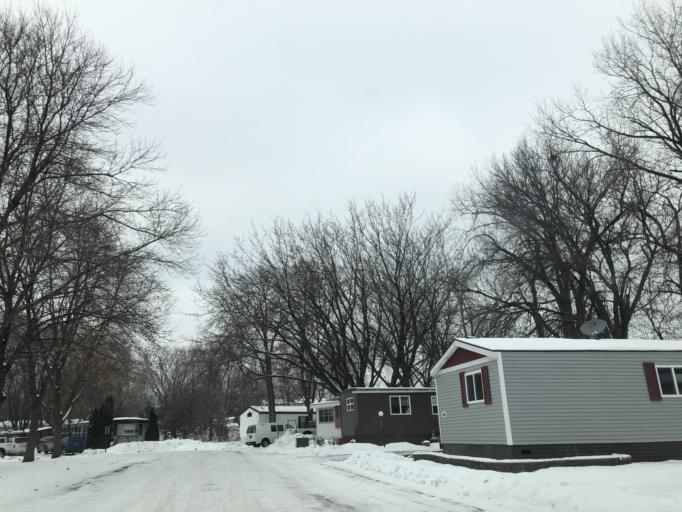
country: US
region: Minnesota
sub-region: Ramsey County
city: New Brighton
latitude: 45.0824
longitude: -93.1815
